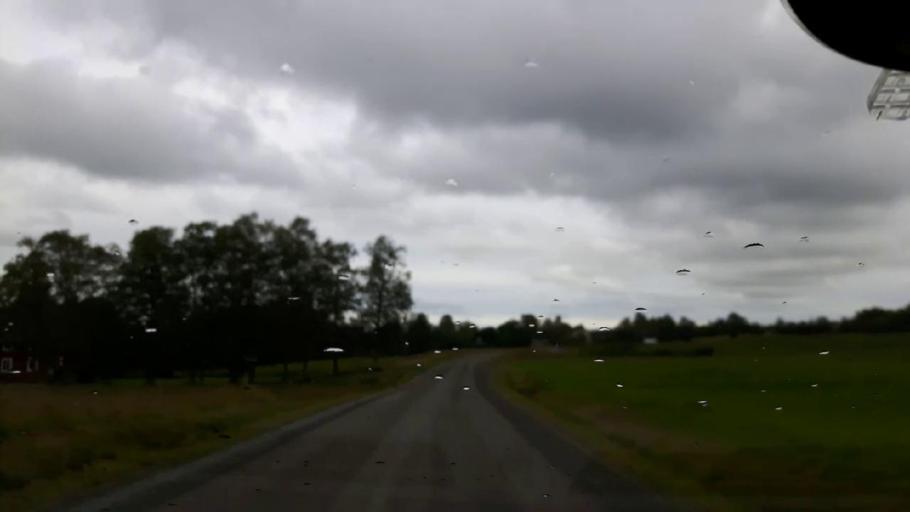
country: SE
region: Jaemtland
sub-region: OEstersunds Kommun
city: Ostersund
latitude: 63.0316
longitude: 14.5797
